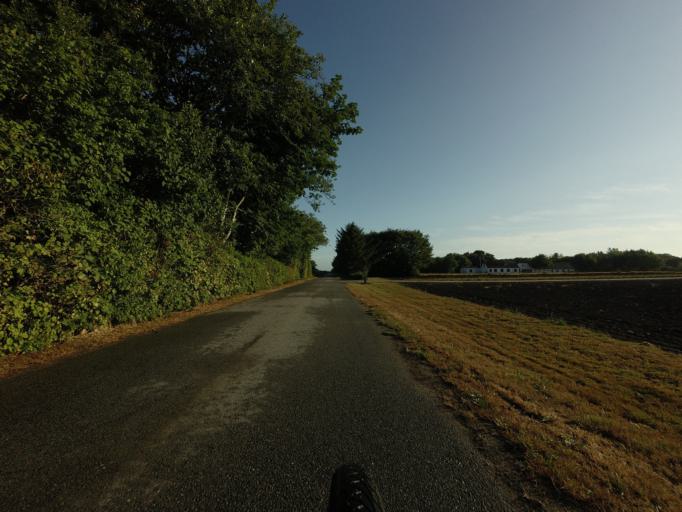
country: DK
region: North Denmark
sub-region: Hjorring Kommune
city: Vra
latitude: 57.3619
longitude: 9.8658
